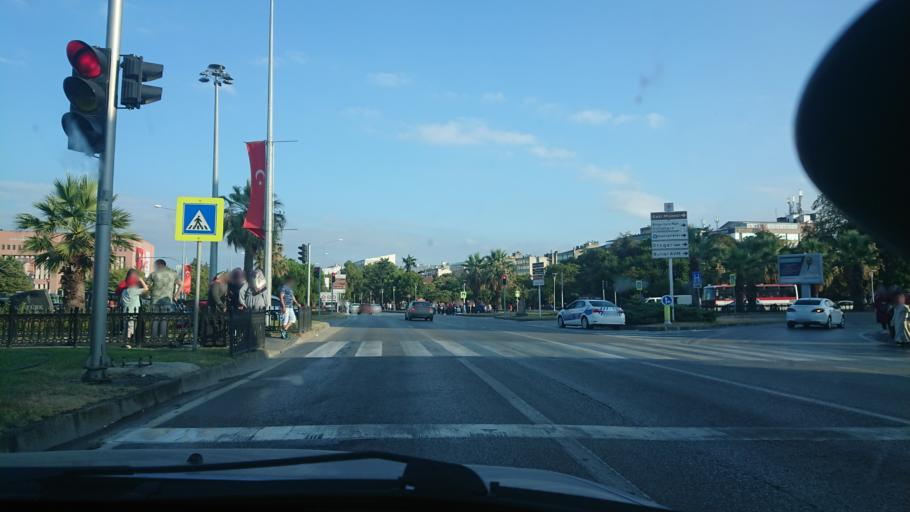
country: TR
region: Samsun
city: Samsun
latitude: 41.2911
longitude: 36.3356
